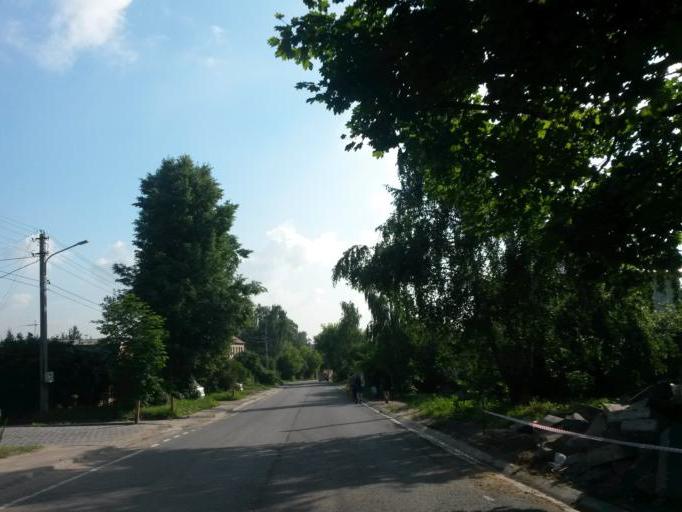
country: RU
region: Moscow
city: Zyablikovo
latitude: 55.6144
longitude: 37.7859
